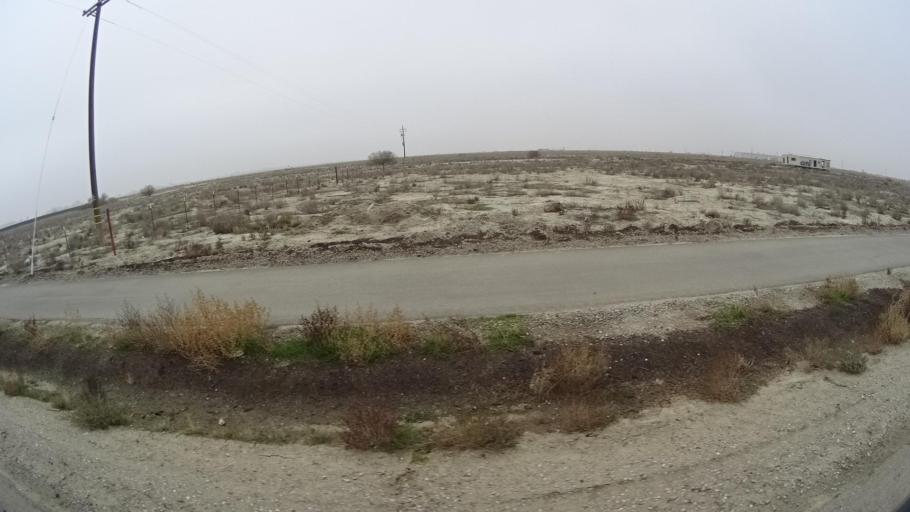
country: US
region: California
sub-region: Kern County
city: Rosedale
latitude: 35.2438
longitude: -119.2528
